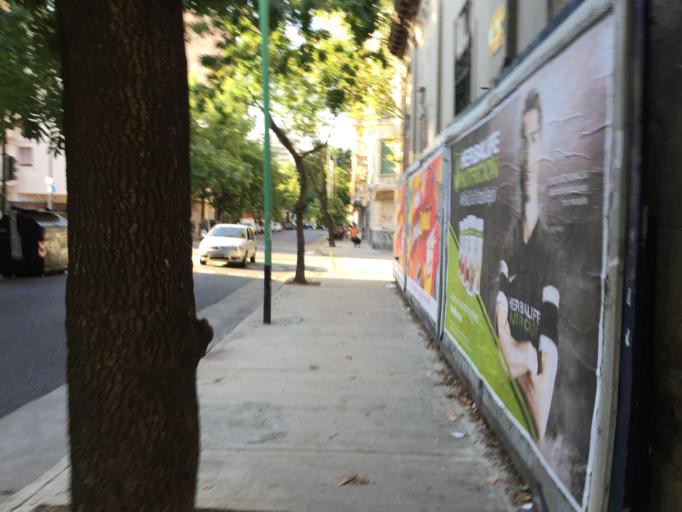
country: AR
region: Buenos Aires F.D.
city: Buenos Aires
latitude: -34.6211
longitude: -58.3985
